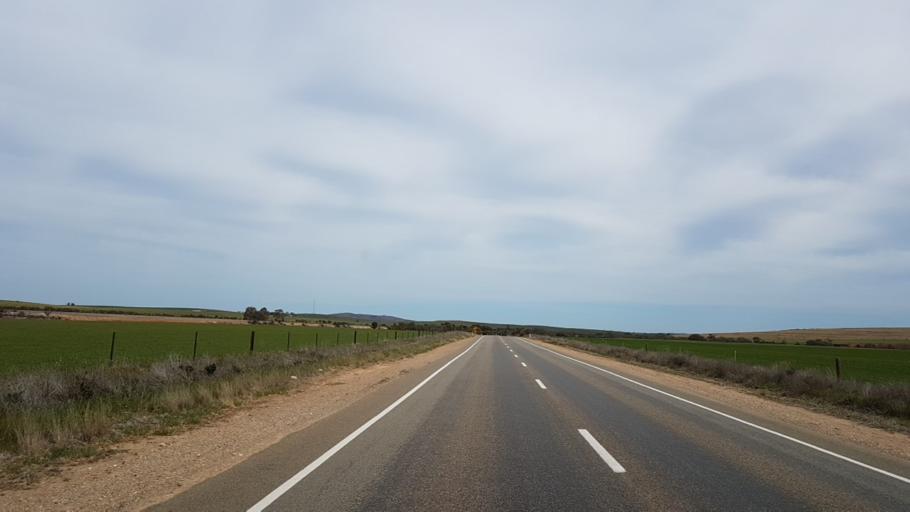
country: AU
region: South Australia
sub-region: Northern Areas
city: Jamestown
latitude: -33.2296
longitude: 138.3940
